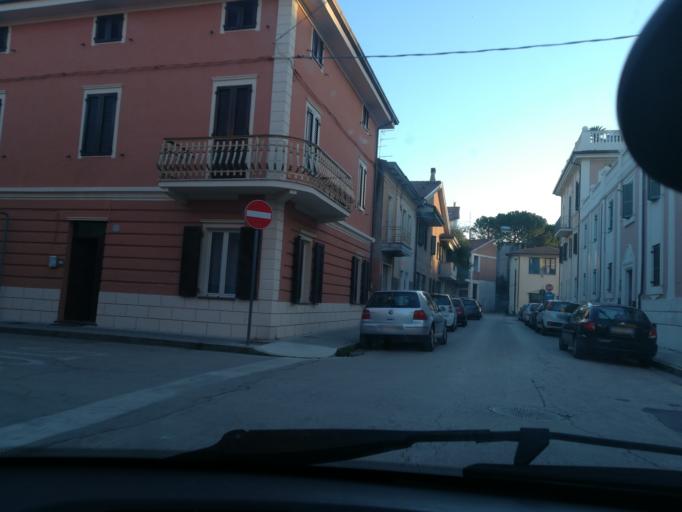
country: IT
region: The Marches
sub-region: Provincia di Macerata
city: Portocivitanova
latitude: 43.3033
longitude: 13.7336
